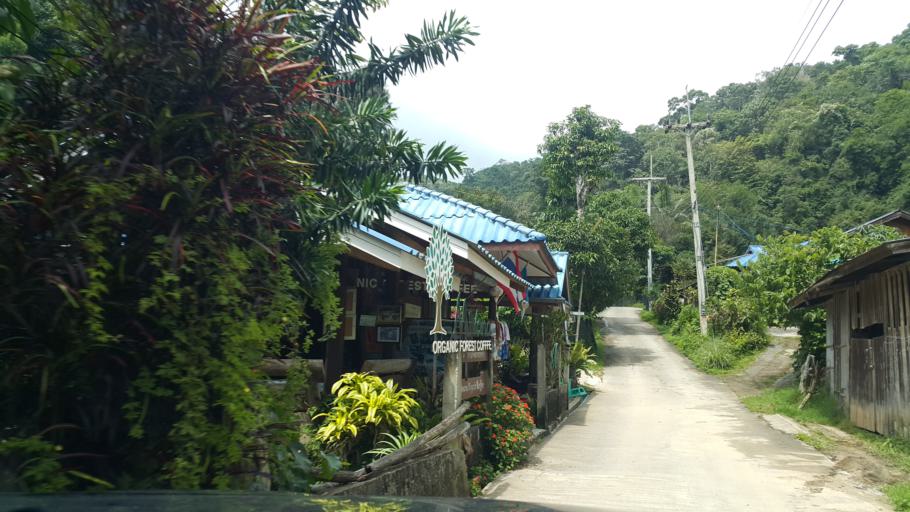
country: TH
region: Lampang
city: Wang Nuea
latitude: 19.0898
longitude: 99.3720
